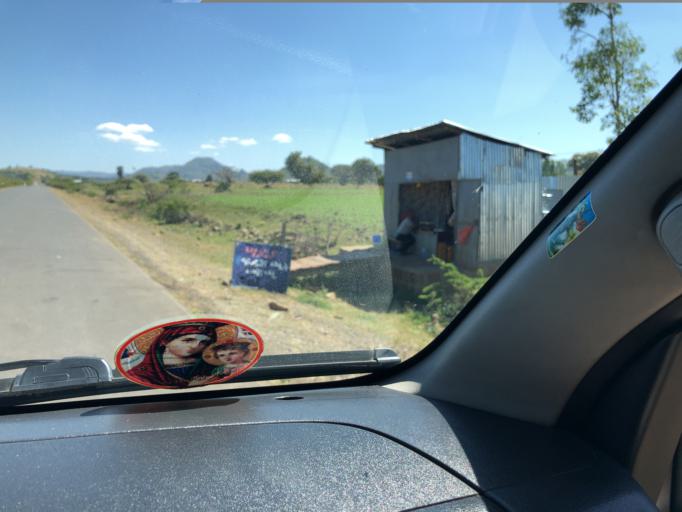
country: ET
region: Amhara
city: Werota
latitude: 11.9385
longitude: 37.7767
